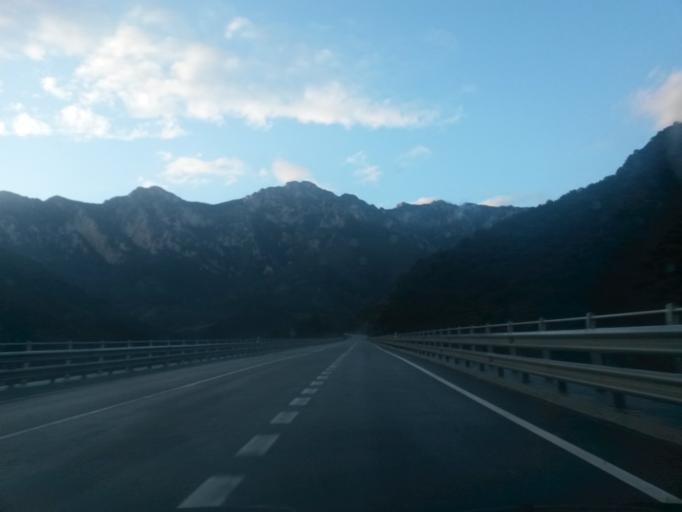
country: ES
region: Catalonia
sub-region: Provincia de Barcelona
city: Baga
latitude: 42.2730
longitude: 1.8537
